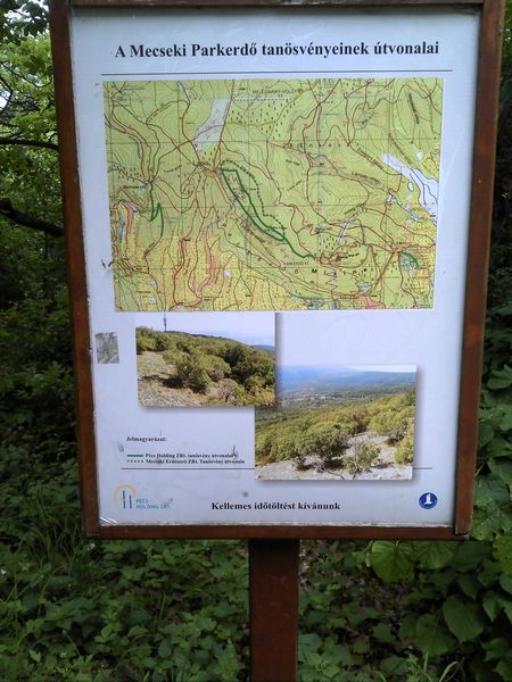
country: HU
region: Baranya
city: Pecs
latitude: 46.0995
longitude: 18.2319
